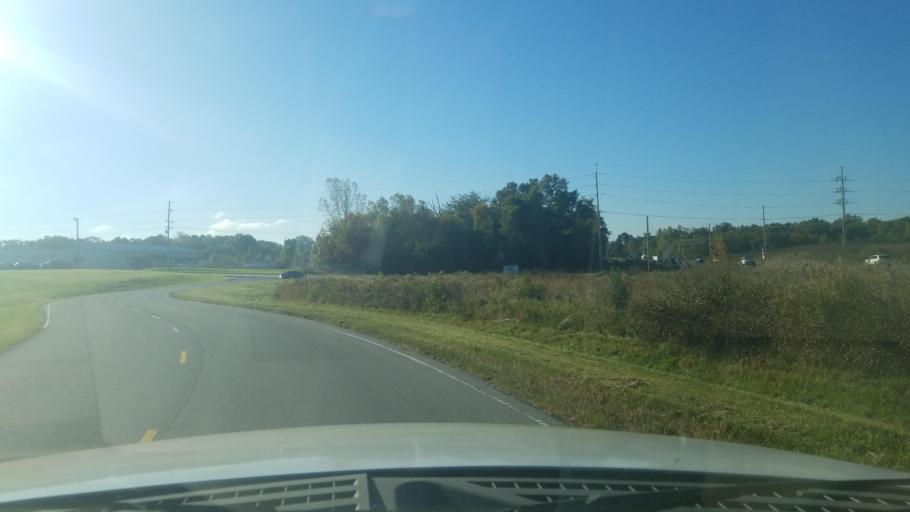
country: US
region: Illinois
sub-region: Williamson County
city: Energy
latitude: 37.7424
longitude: -89.0212
